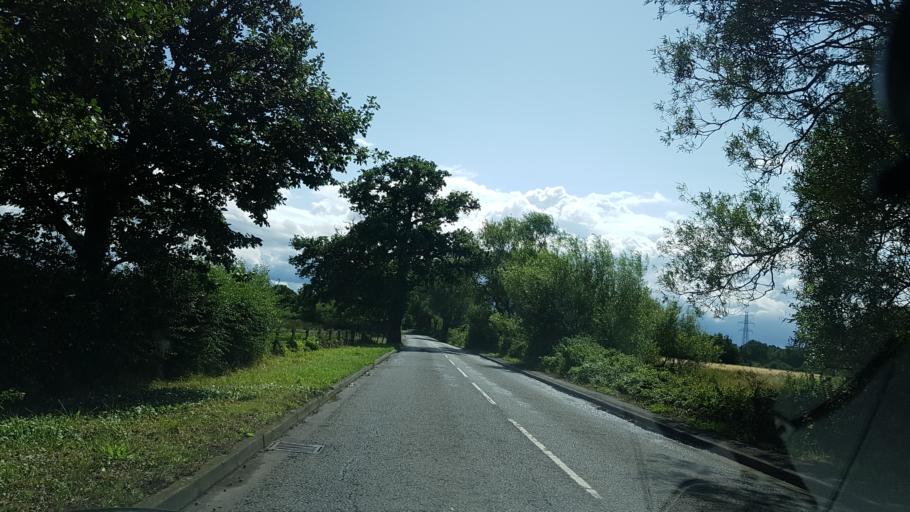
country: GB
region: England
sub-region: Surrey
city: Ripley
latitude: 51.3117
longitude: -0.5108
